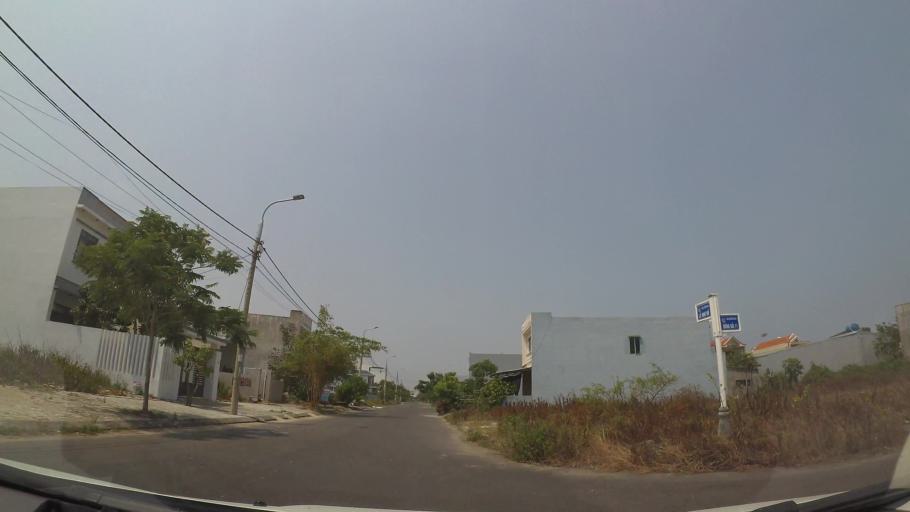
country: VN
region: Da Nang
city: Ngu Hanh Son
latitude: 15.9880
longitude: 108.2694
